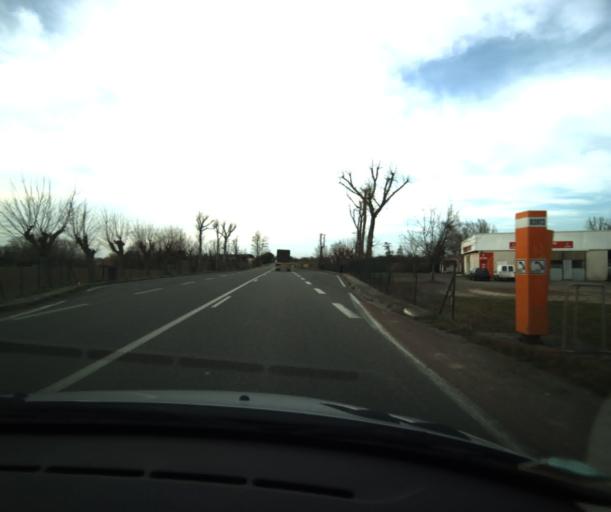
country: FR
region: Midi-Pyrenees
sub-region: Departement du Tarn-et-Garonne
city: Saint-Porquier
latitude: 43.9965
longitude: 1.1869
